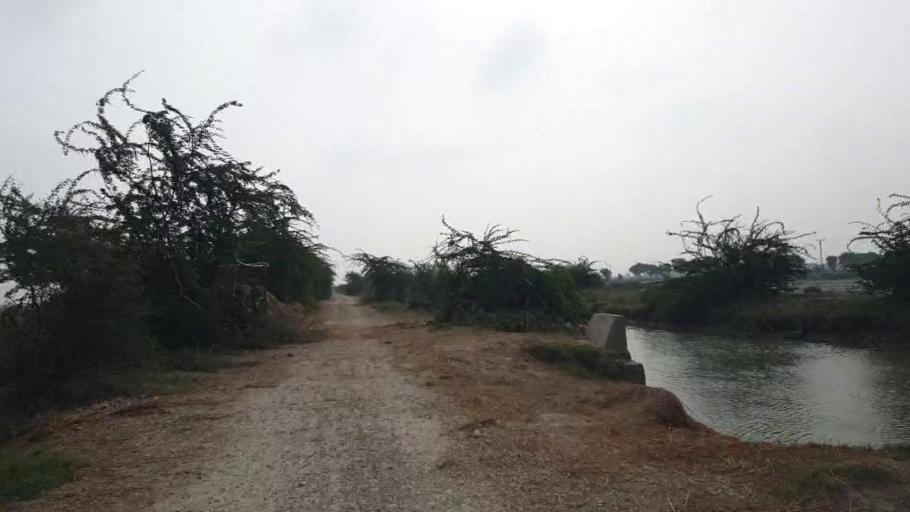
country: PK
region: Sindh
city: Kario
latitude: 24.8600
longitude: 68.5220
